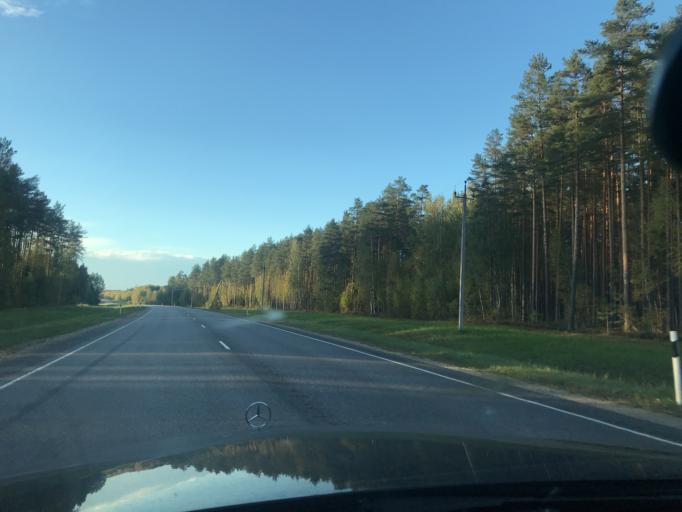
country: EE
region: Vorumaa
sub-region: Voru linn
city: Voru
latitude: 57.8386
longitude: 27.0561
